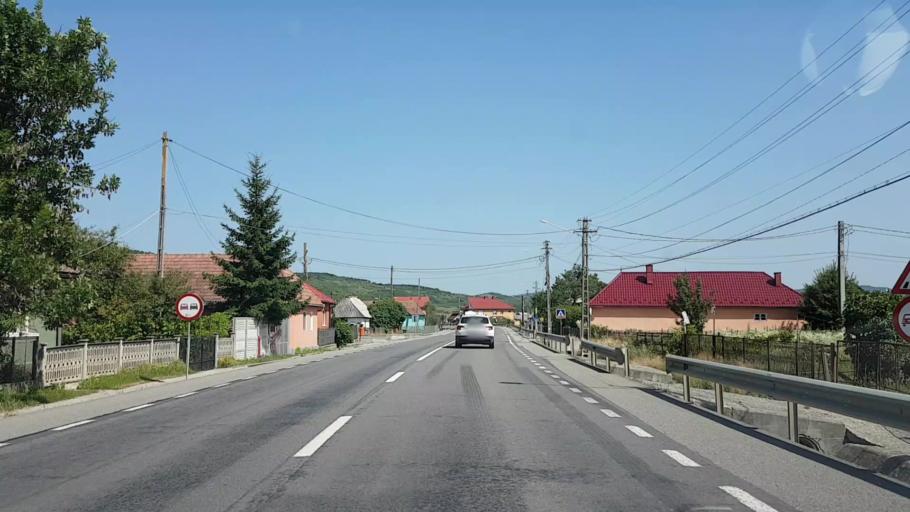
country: RO
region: Bistrita-Nasaud
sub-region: Comuna Sintereag
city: Sintereag
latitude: 47.1793
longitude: 24.2934
